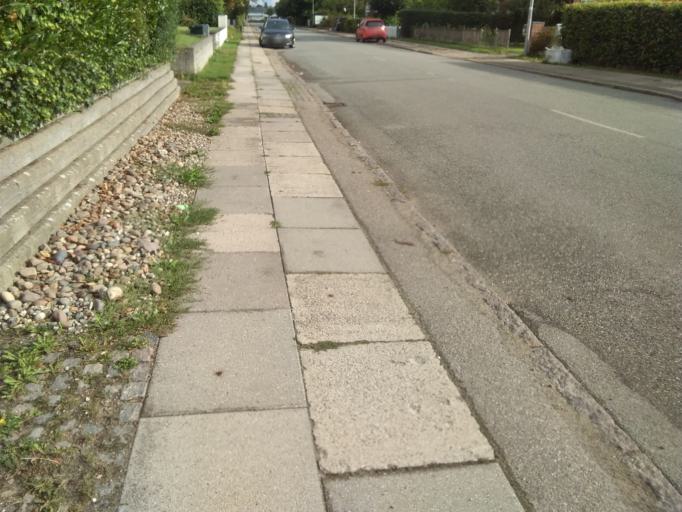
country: DK
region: Capital Region
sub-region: Gladsaxe Municipality
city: Buddinge
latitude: 55.7283
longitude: 12.5070
